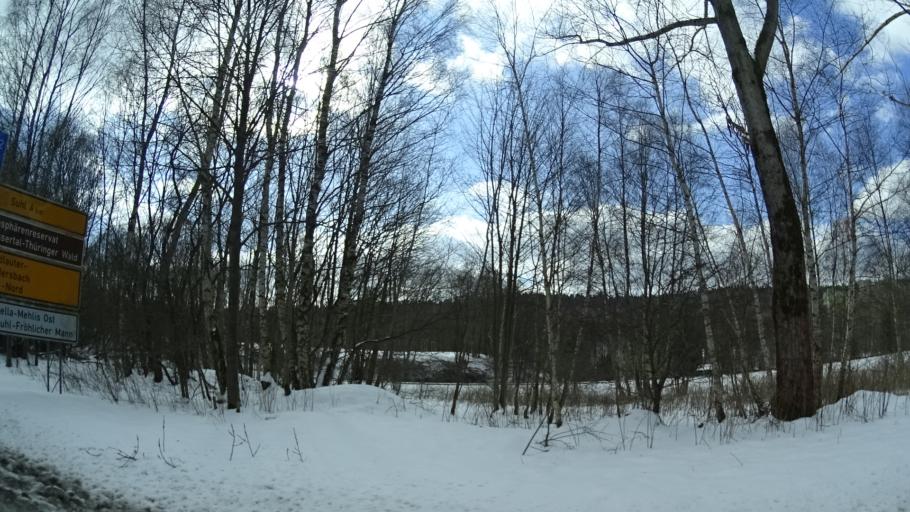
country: DE
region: Thuringia
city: Suhl
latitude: 50.6398
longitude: 10.6938
